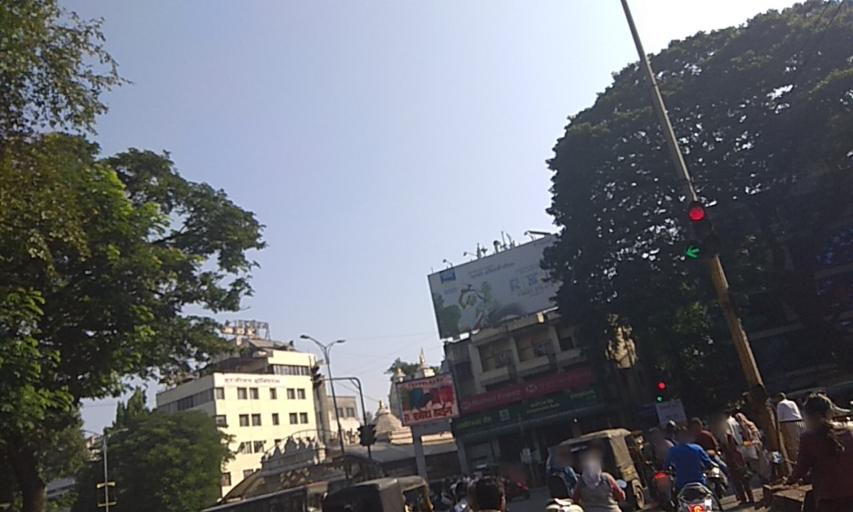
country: IN
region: Maharashtra
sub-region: Pune Division
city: Pune
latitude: 18.4997
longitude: 73.8536
